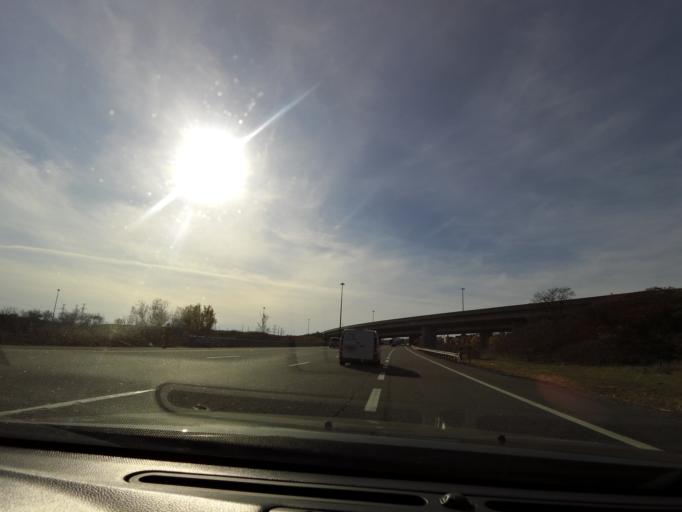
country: CA
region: Ontario
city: Burlington
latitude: 43.3386
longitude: -79.8297
